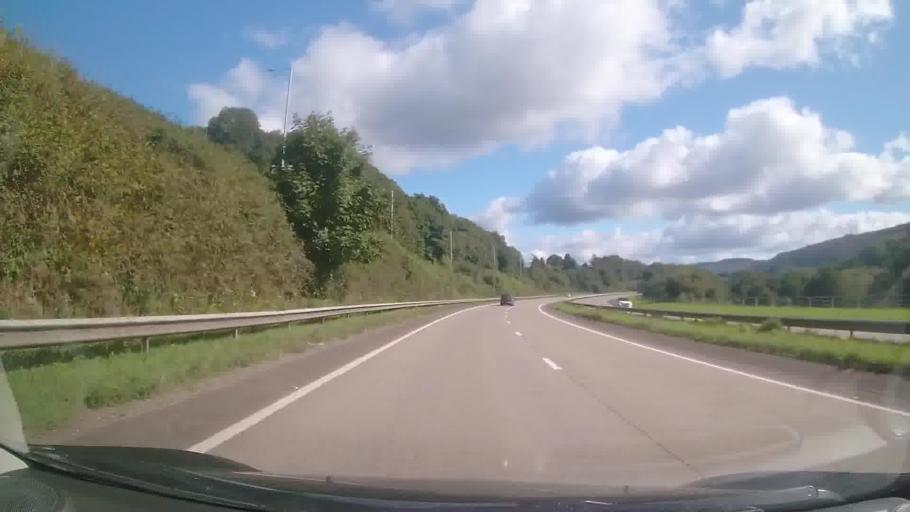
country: GB
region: Wales
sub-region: Neath Port Talbot
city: Neath
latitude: 51.6812
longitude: -3.7751
